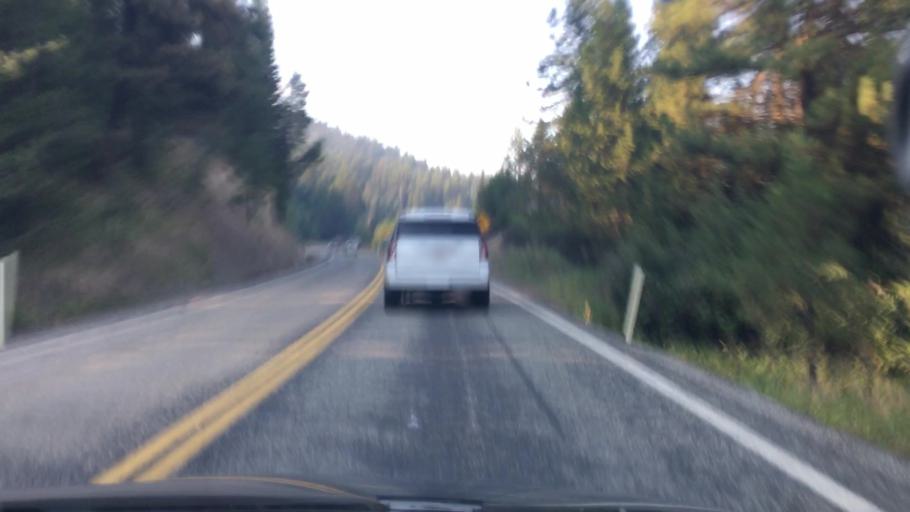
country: US
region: Idaho
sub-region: Valley County
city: Cascade
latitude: 44.3050
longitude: -116.0875
